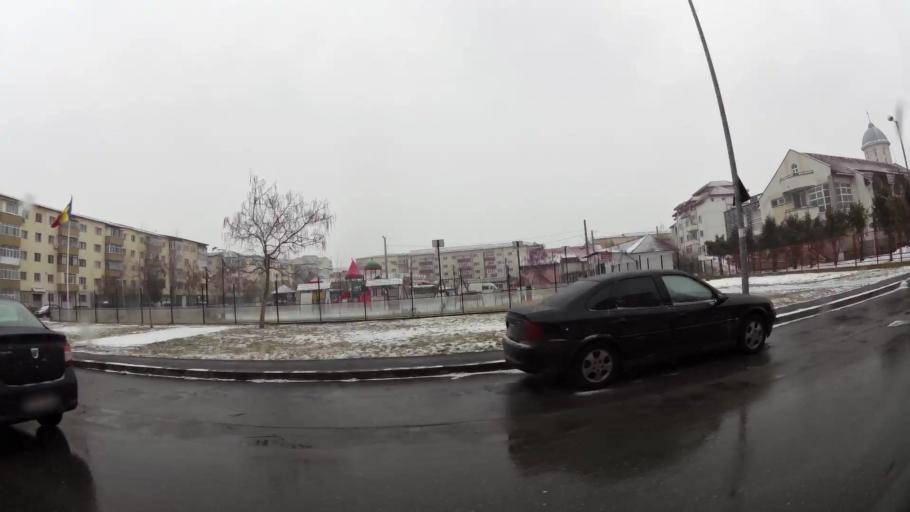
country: RO
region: Dambovita
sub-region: Municipiul Targoviste
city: Targoviste
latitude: 44.9169
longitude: 25.4780
